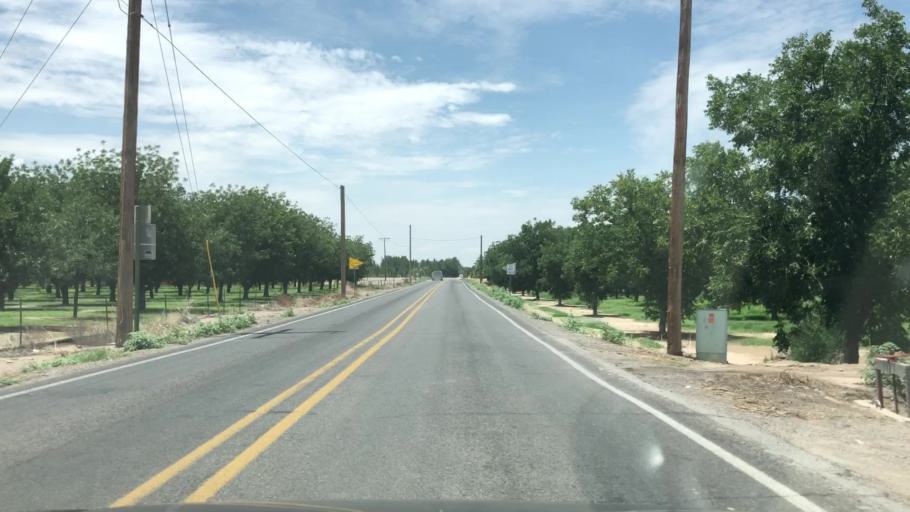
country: US
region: New Mexico
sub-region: Dona Ana County
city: Vado
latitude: 32.1150
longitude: -106.6663
